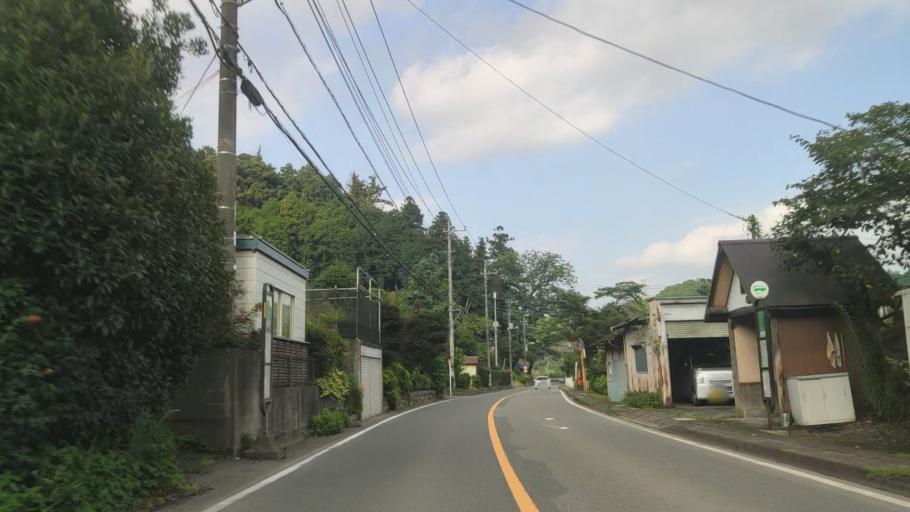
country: JP
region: Tokyo
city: Ome
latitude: 35.8297
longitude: 139.2640
